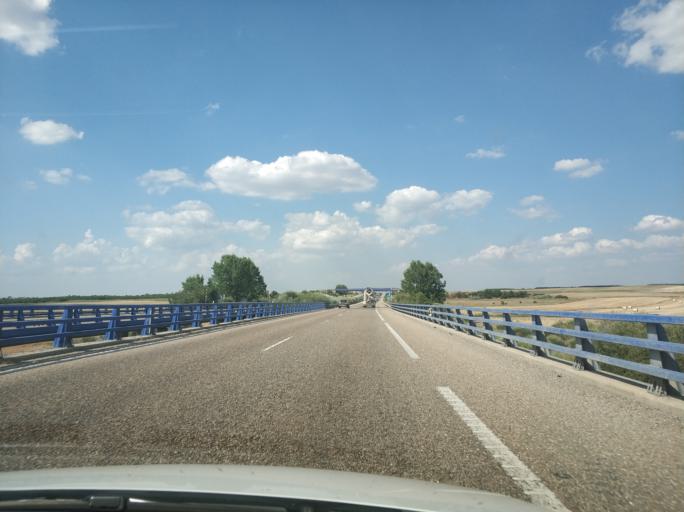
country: ES
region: Castille and Leon
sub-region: Provincia de Zamora
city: Matilla de Arzon
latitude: 42.1167
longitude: -5.6565
